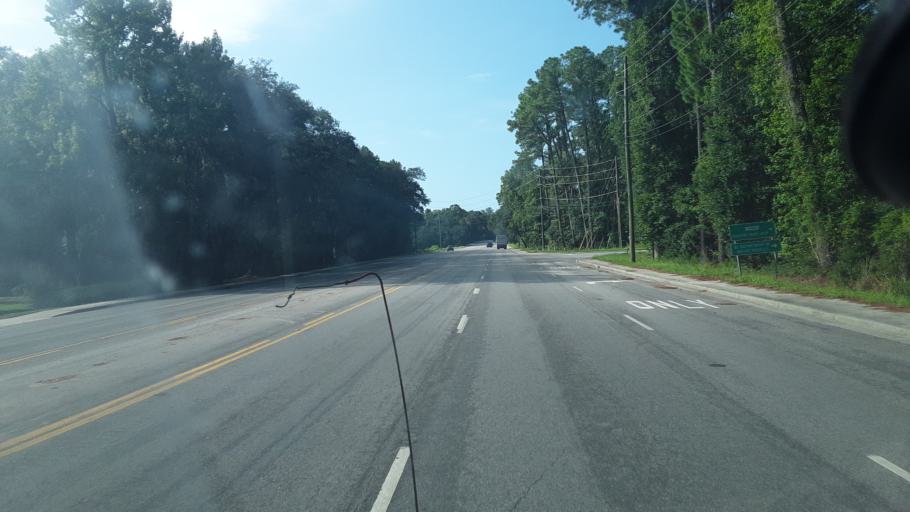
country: US
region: South Carolina
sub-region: Beaufort County
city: Burton
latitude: 32.4196
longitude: -80.7306
